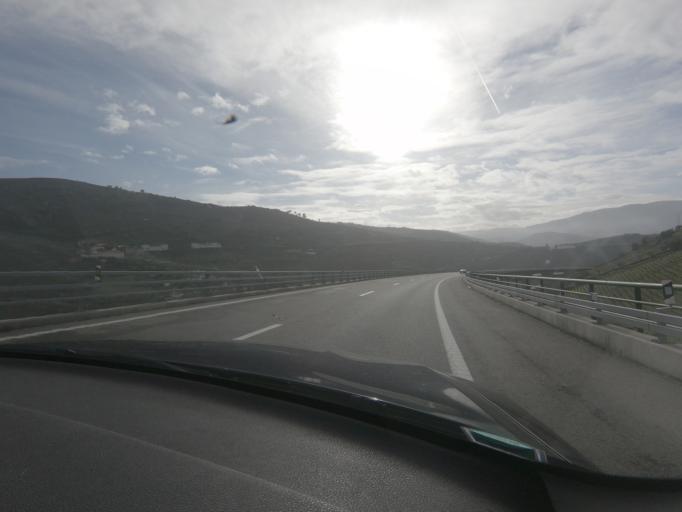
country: PT
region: Vila Real
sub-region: Peso da Regua
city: Peso da Regua
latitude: 41.1759
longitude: -7.7512
